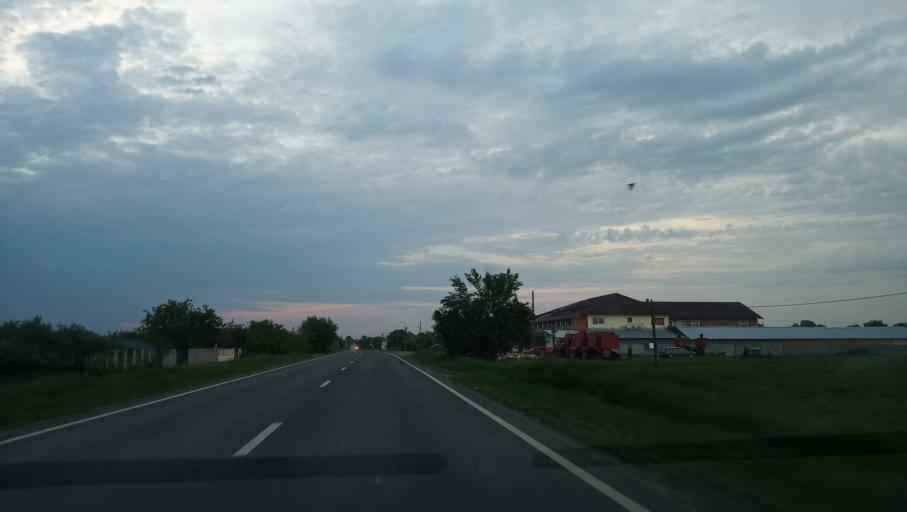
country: RO
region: Timis
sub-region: Comuna Jebel
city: Jebel
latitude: 45.5497
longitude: 21.2231
